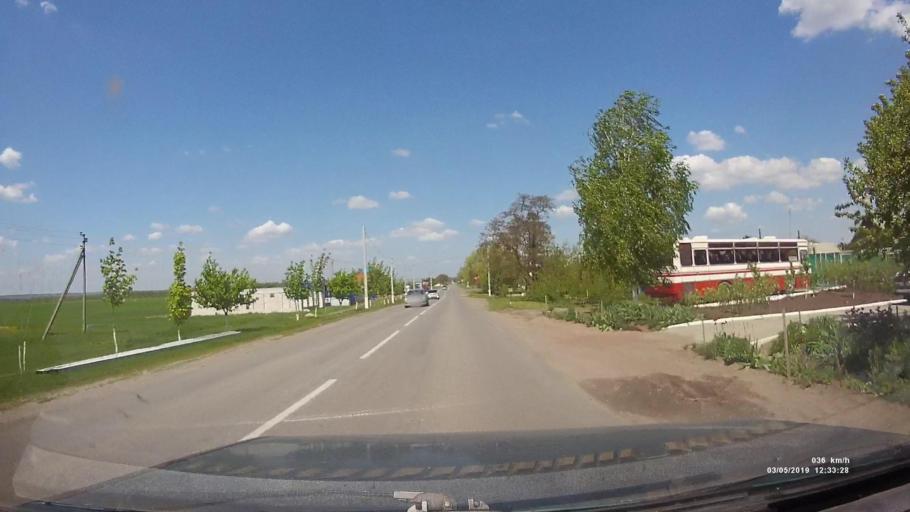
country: RU
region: Rostov
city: Semikarakorsk
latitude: 47.5132
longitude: 40.7717
